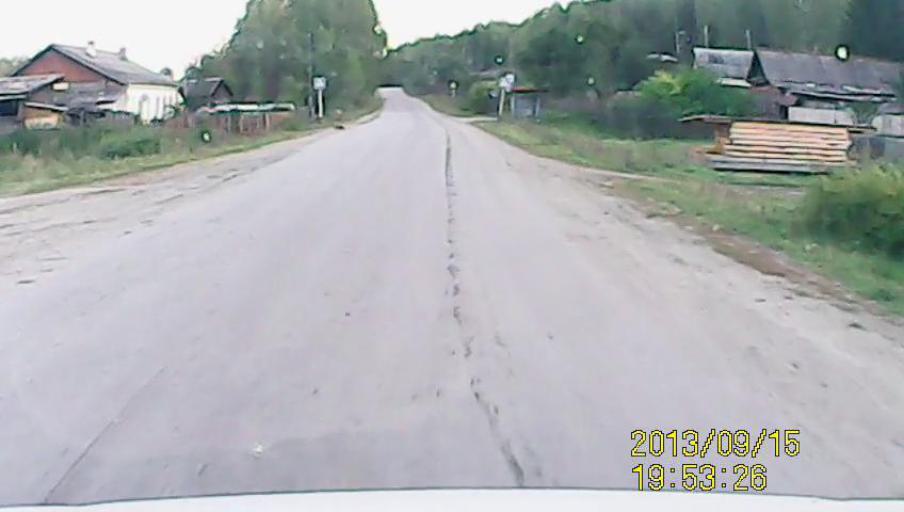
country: RU
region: Chelyabinsk
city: Kyshtym
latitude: 55.7640
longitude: 60.4857
